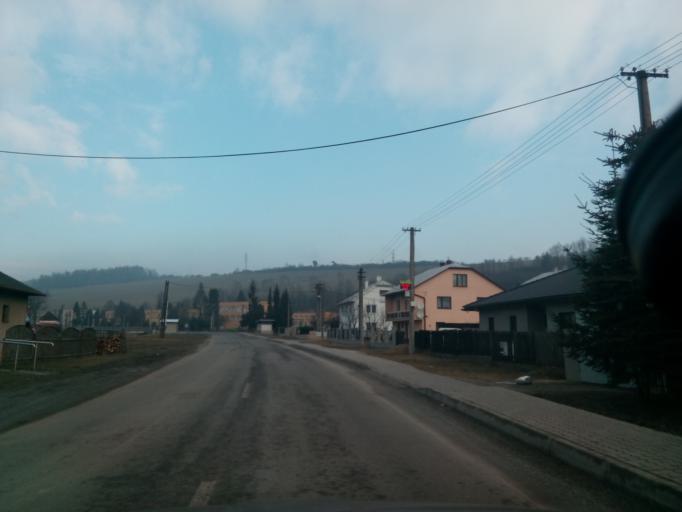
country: SK
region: Presovsky
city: Lipany
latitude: 49.1722
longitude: 20.8705
